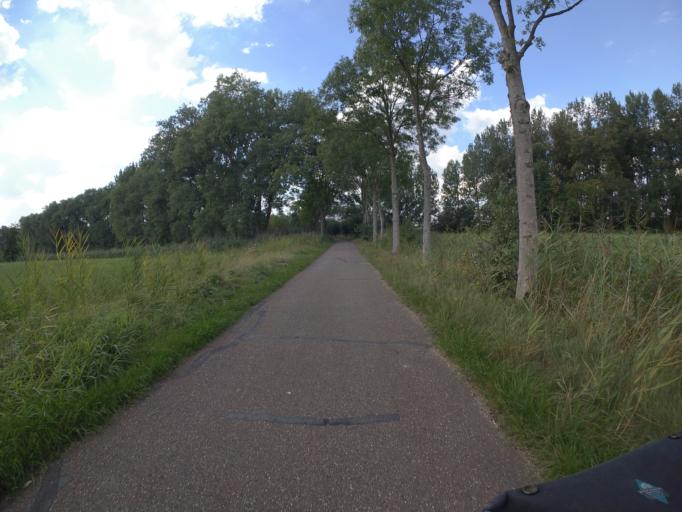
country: NL
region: North Brabant
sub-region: Gemeente Schijndel
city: Schijndel
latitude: 51.6483
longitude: 5.4563
